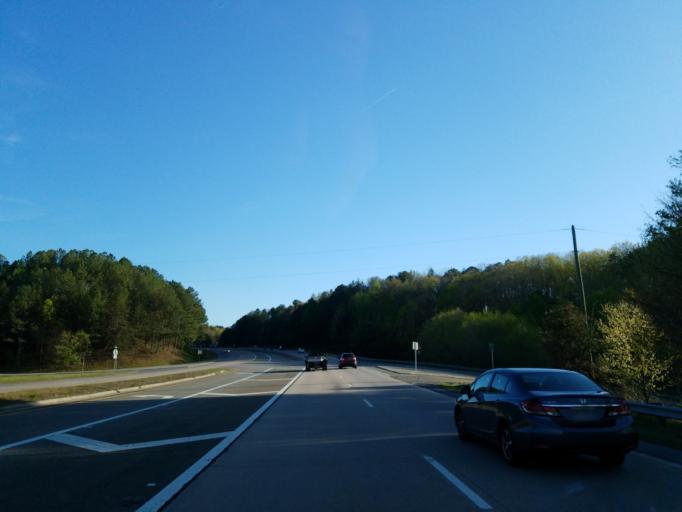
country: US
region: Georgia
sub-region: Gilmer County
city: Ellijay
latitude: 34.5661
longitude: -84.5216
